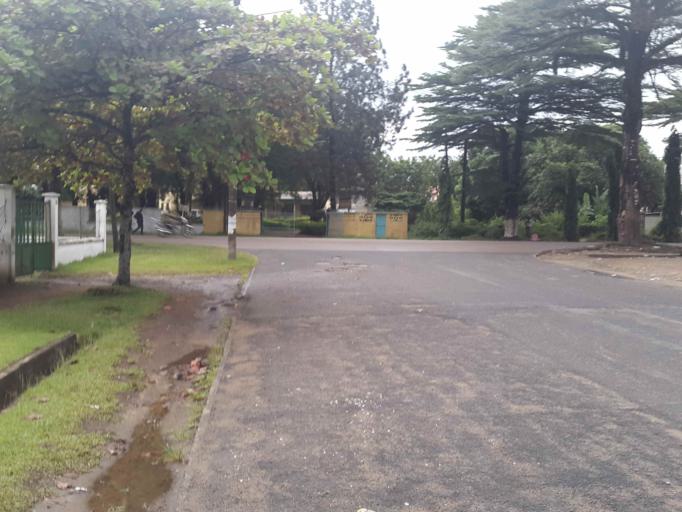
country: CM
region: Littoral
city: Douala
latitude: 4.0895
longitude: 9.7383
